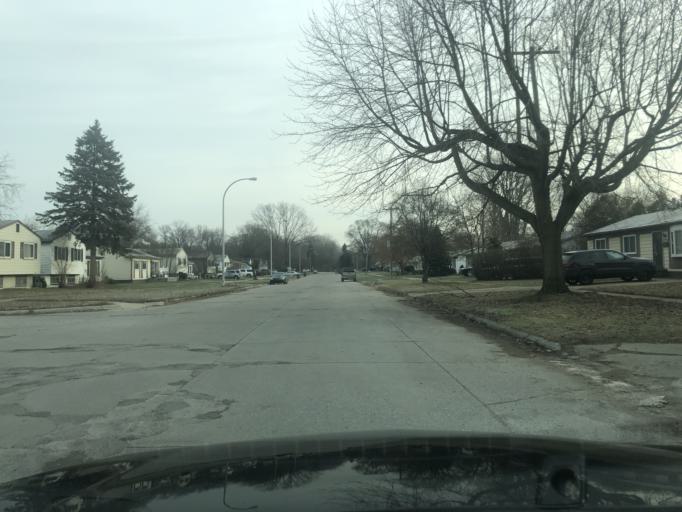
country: US
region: Michigan
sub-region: Wayne County
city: Taylor
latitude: 42.1879
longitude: -83.3146
